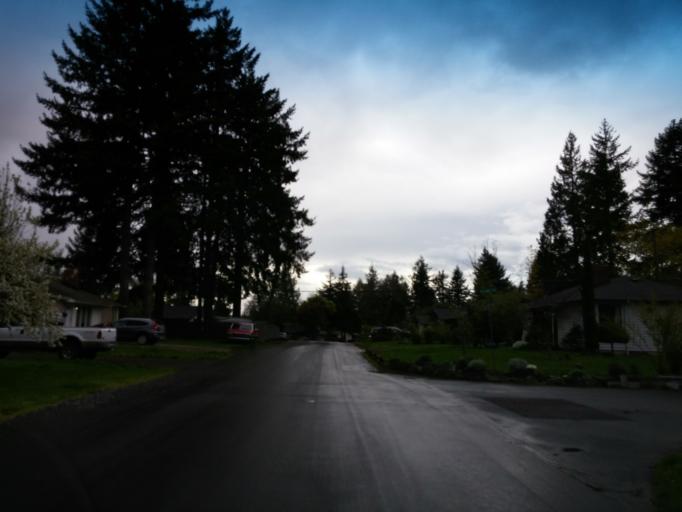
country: US
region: Oregon
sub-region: Washington County
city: Cedar Mill
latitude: 45.5177
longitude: -122.8205
